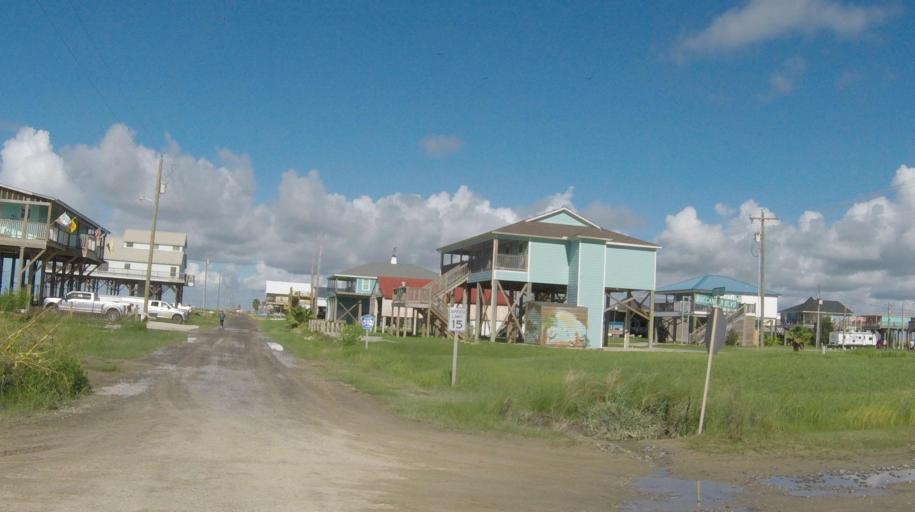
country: US
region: Louisiana
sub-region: Cameron Parish
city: Cameron
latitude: 29.7701
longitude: -93.4542
